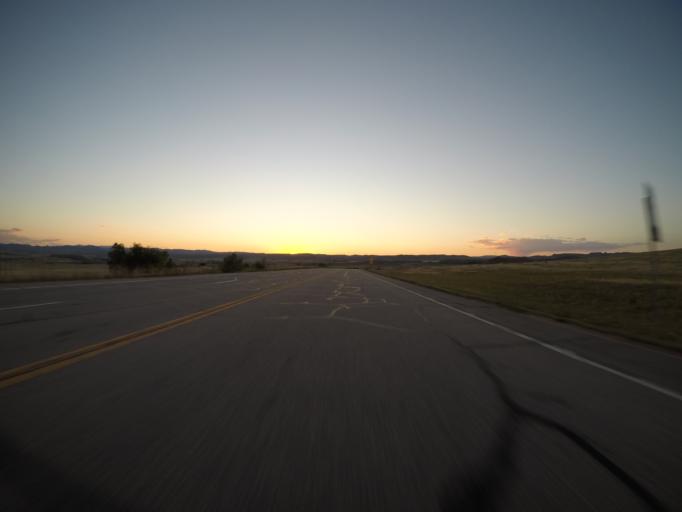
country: US
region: Colorado
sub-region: Larimer County
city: Laporte
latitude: 40.7988
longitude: -105.2259
